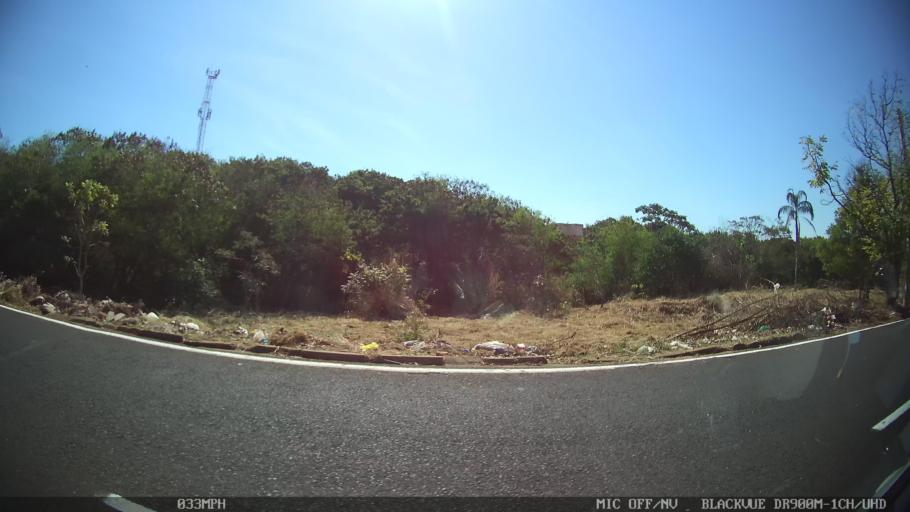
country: BR
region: Sao Paulo
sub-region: Sao Jose Do Rio Preto
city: Sao Jose do Rio Preto
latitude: -20.7741
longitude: -49.4092
